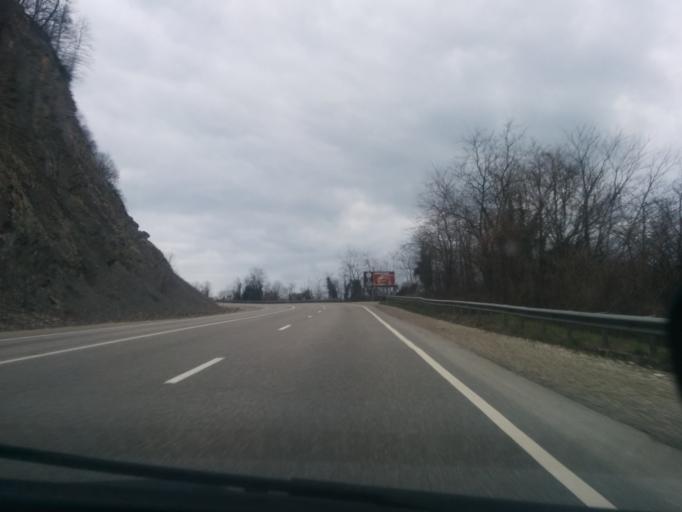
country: RU
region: Krasnodarskiy
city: Nebug
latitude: 44.1749
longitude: 38.9765
